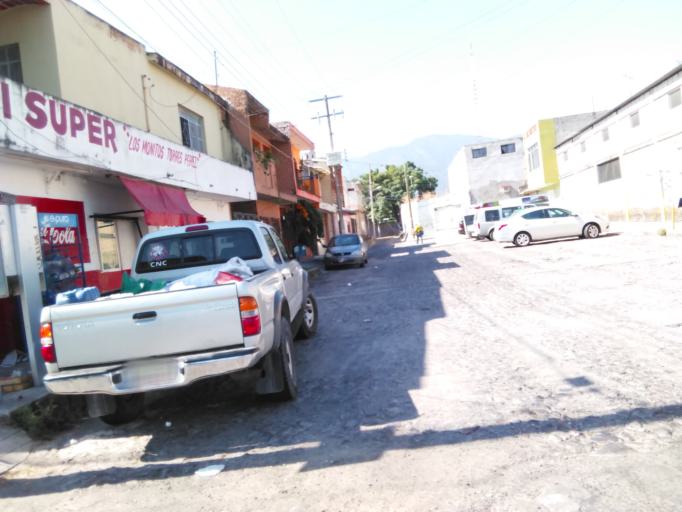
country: MX
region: Nayarit
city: Tepic
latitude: 21.4938
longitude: -104.8886
